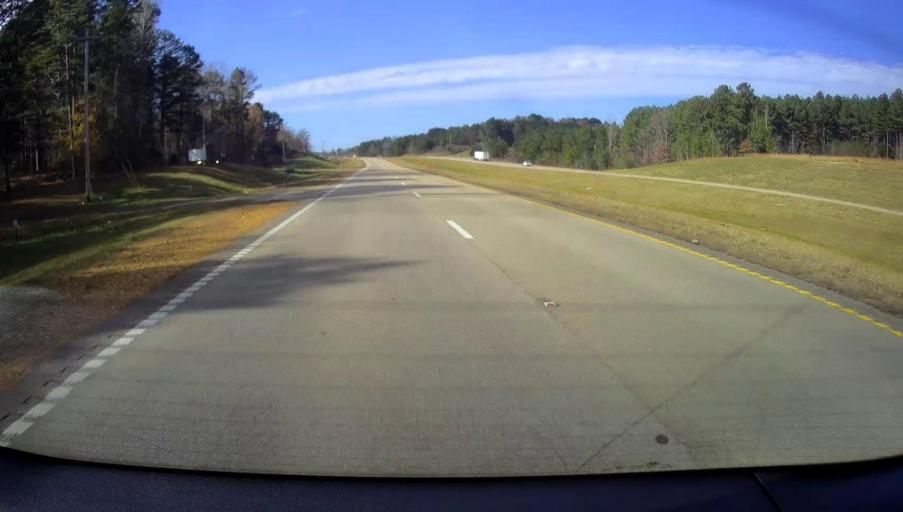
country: US
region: Mississippi
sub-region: Tippah County
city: Ripley
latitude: 34.9531
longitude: -88.9506
